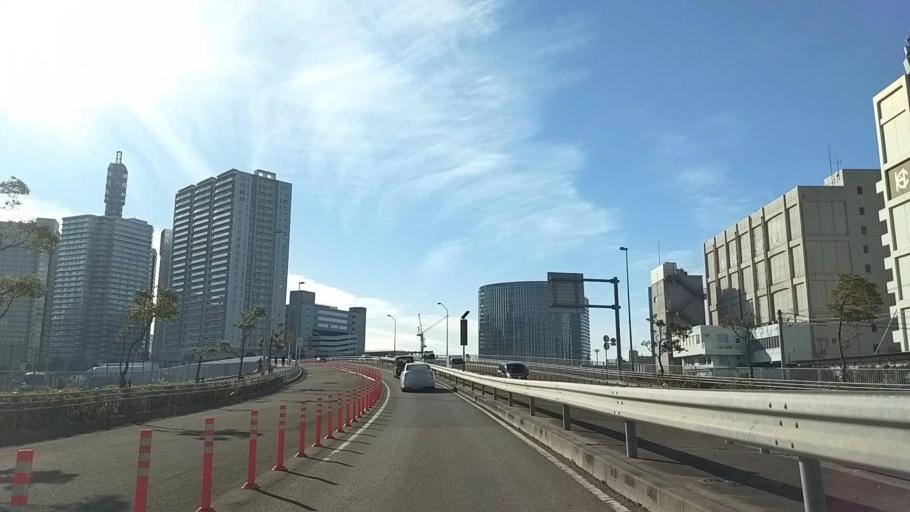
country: JP
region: Kanagawa
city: Yokohama
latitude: 35.4658
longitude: 139.6358
